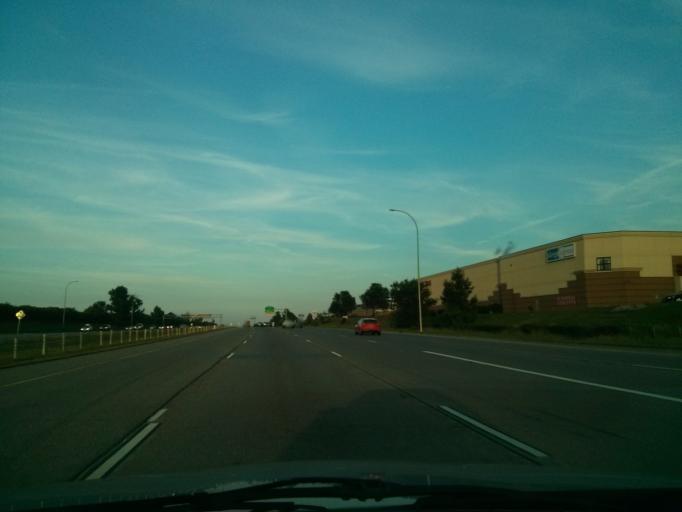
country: US
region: Minnesota
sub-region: Washington County
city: Oakdale
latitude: 44.9485
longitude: -92.9533
